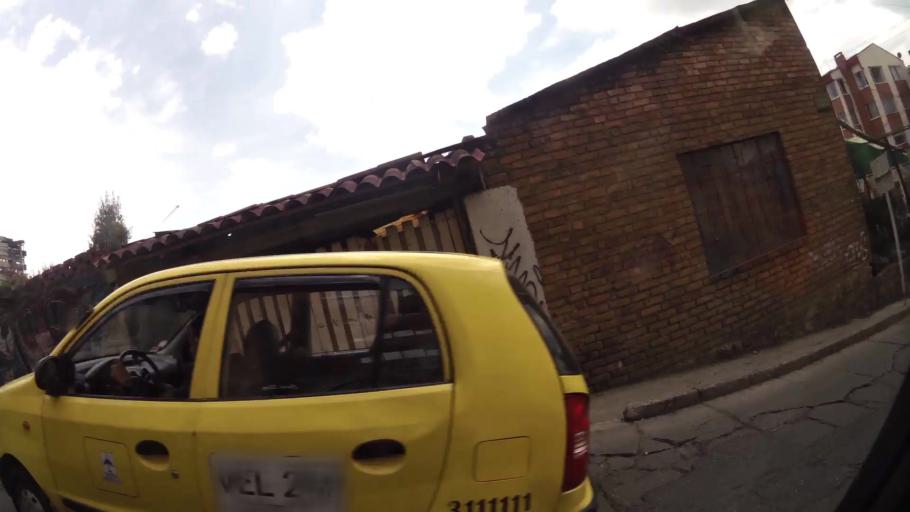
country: CO
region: Cundinamarca
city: Cota
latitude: 4.7446
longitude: -74.0843
